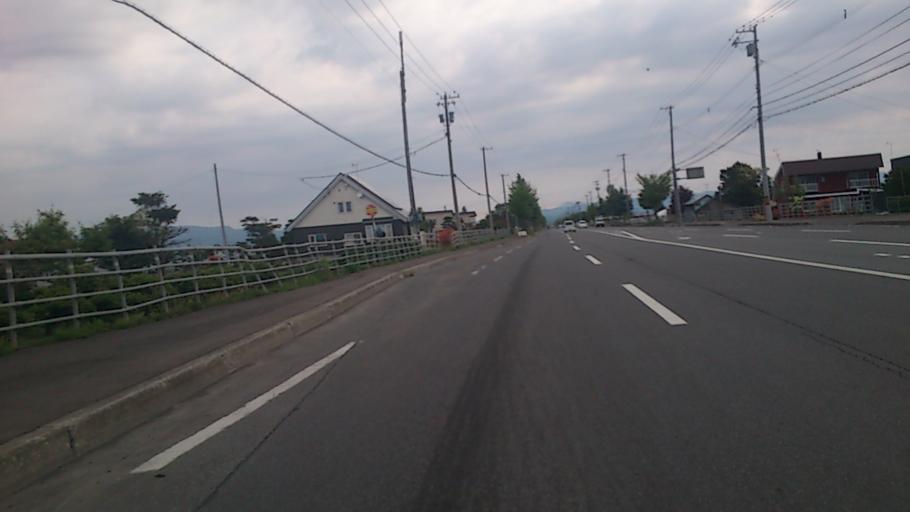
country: JP
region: Hokkaido
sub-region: Asahikawa-shi
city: Asahikawa
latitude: 43.8252
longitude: 142.4573
